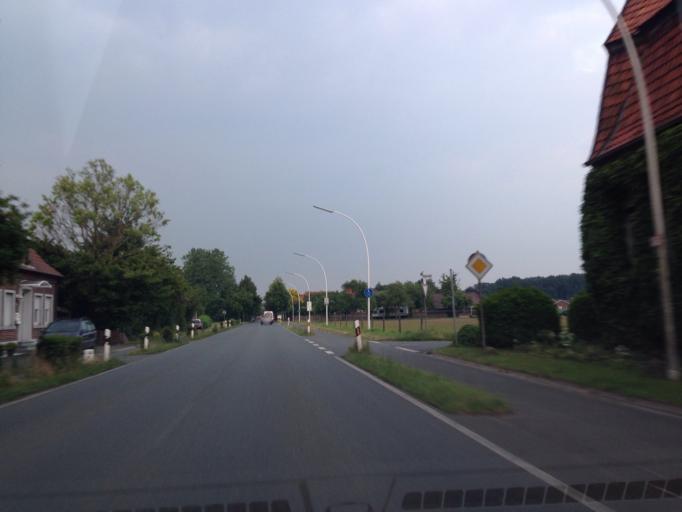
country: DE
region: North Rhine-Westphalia
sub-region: Regierungsbezirk Munster
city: Nottuln
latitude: 51.9030
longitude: 7.4153
